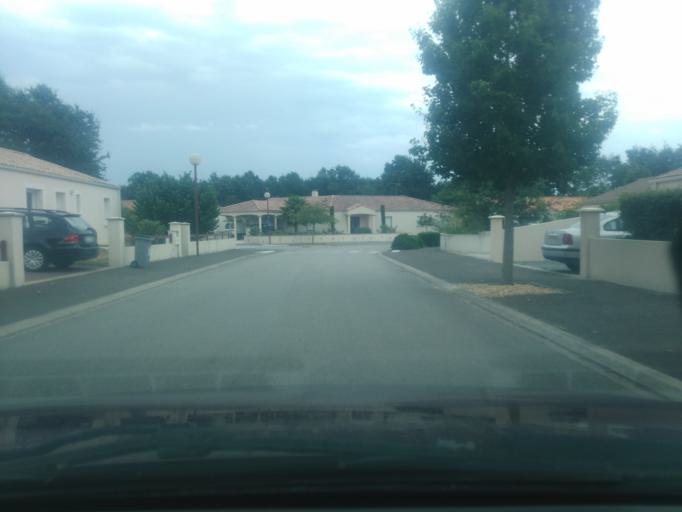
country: FR
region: Pays de la Loire
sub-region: Departement de la Vendee
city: La Ferriere
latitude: 46.7159
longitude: -1.3093
